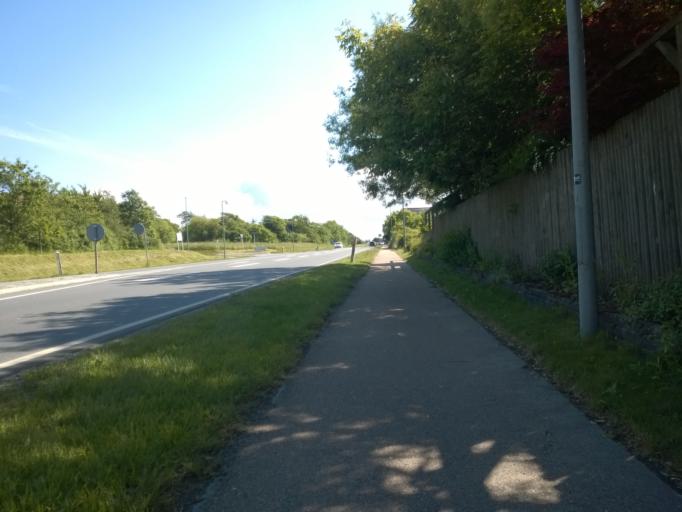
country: DK
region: Central Jutland
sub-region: Holstebro Kommune
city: Vinderup
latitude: 56.4732
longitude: 8.7743
